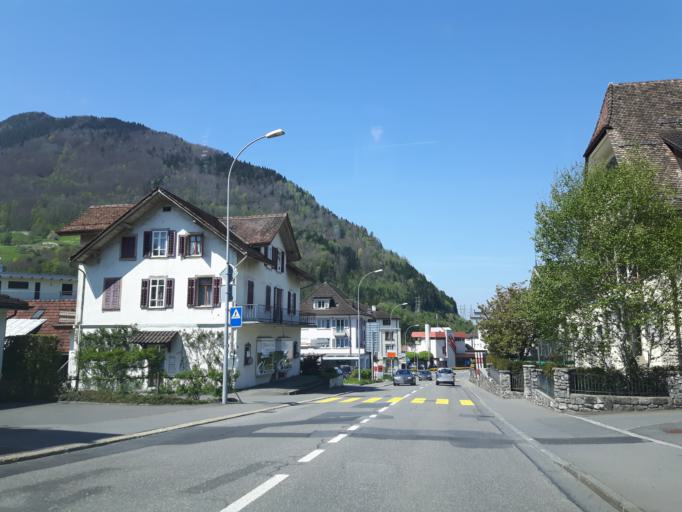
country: CH
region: Schwyz
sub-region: Bezirk Schwyz
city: Ibach
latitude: 47.0257
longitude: 8.6347
